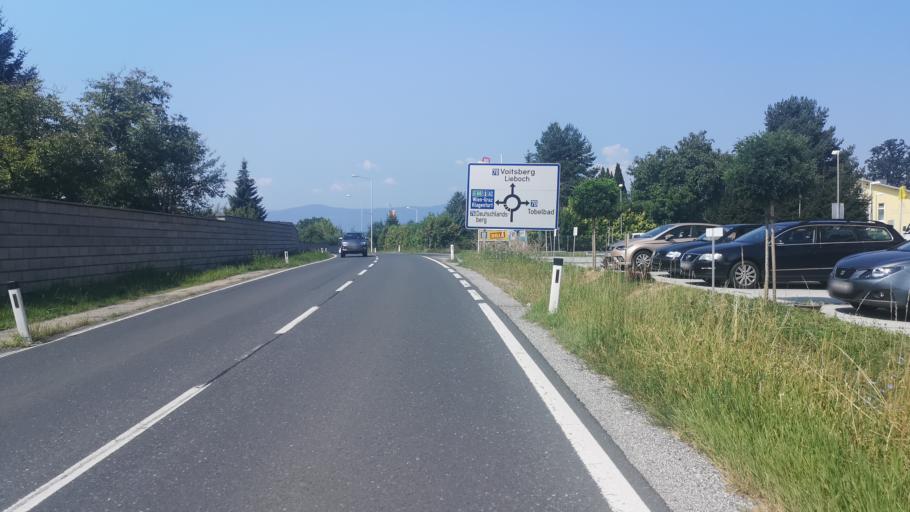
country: AT
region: Styria
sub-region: Politischer Bezirk Graz-Umgebung
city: Lieboch
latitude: 46.9710
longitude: 15.3625
